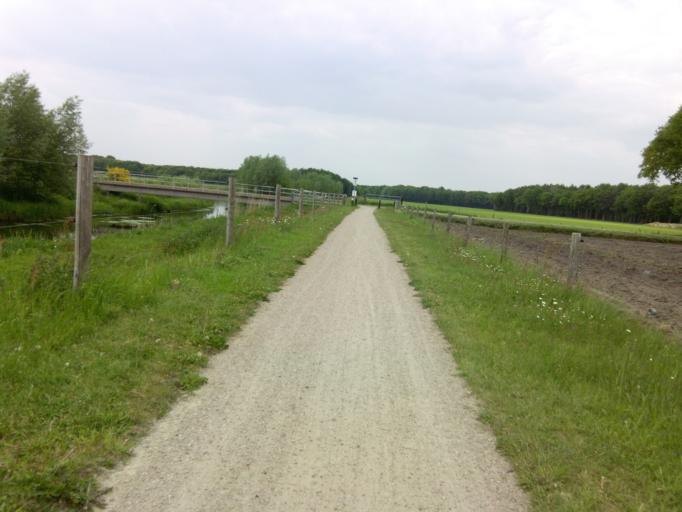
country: NL
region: Gelderland
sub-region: Berkelland
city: Borculo
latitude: 52.0753
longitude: 6.5191
